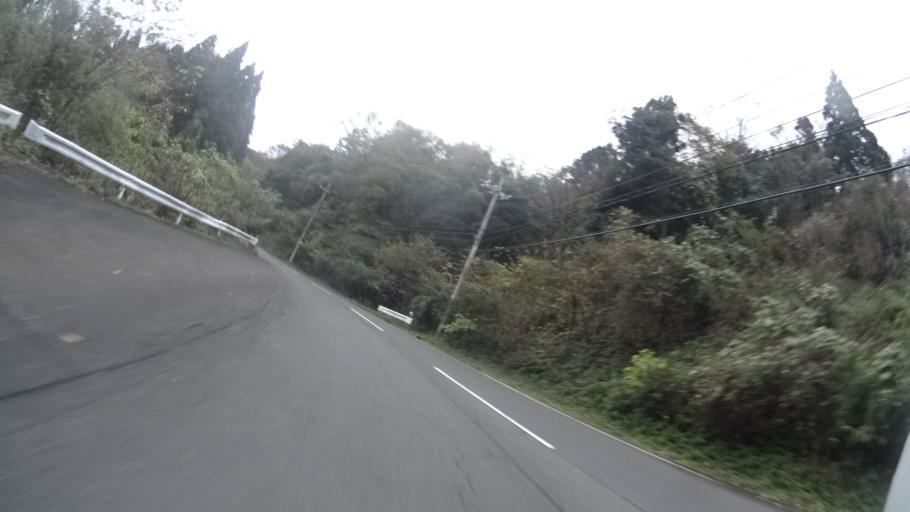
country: JP
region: Kyoto
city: Maizuru
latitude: 35.5537
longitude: 135.4544
